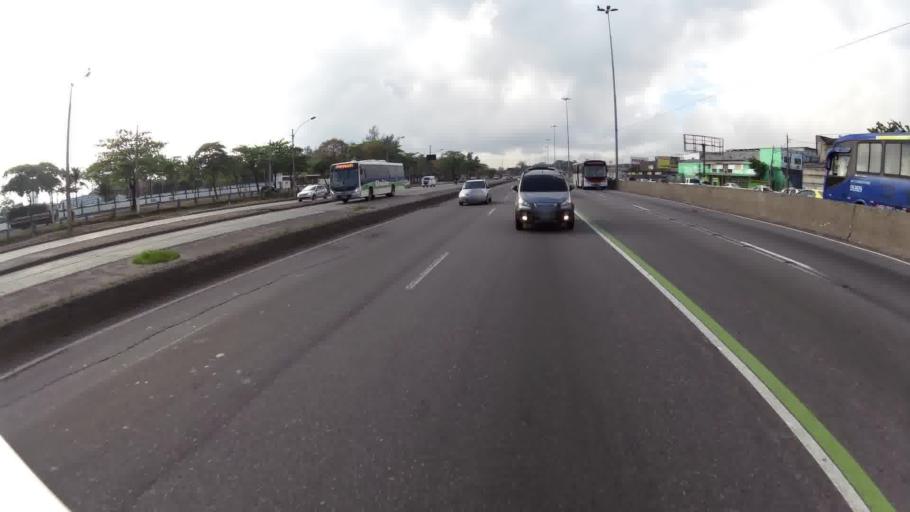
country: BR
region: Rio de Janeiro
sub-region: Duque De Caxias
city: Duque de Caxias
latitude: -22.8282
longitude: -43.2729
